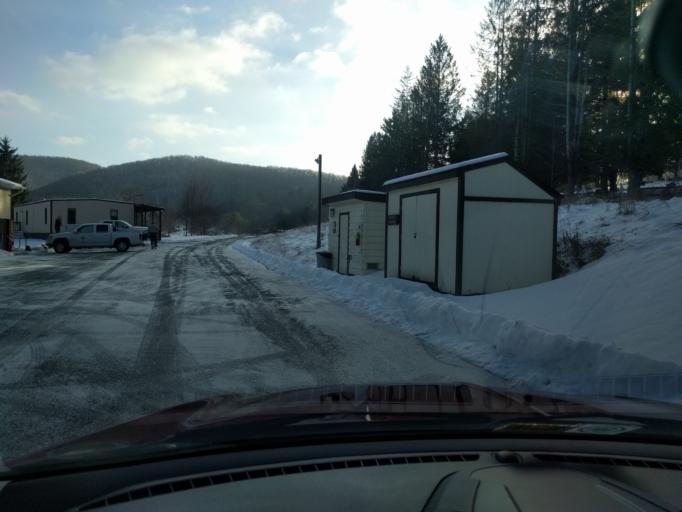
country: US
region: West Virginia
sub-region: Pocahontas County
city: Marlinton
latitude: 38.2150
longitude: -80.0807
